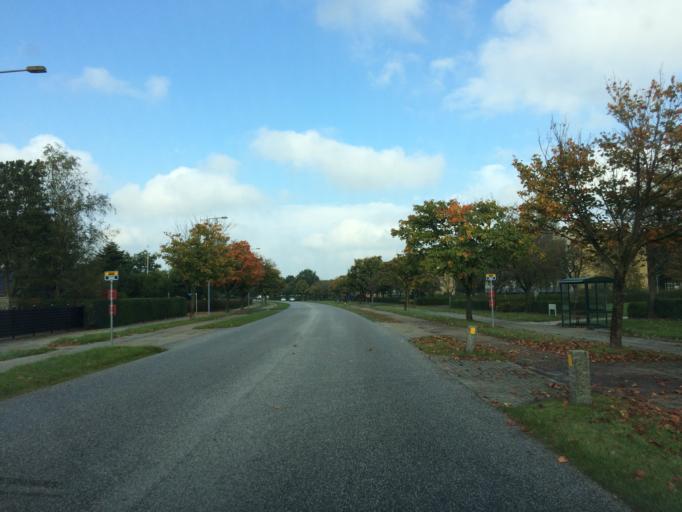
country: DK
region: Central Jutland
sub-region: Skive Kommune
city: Skive
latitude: 56.5439
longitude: 9.0232
